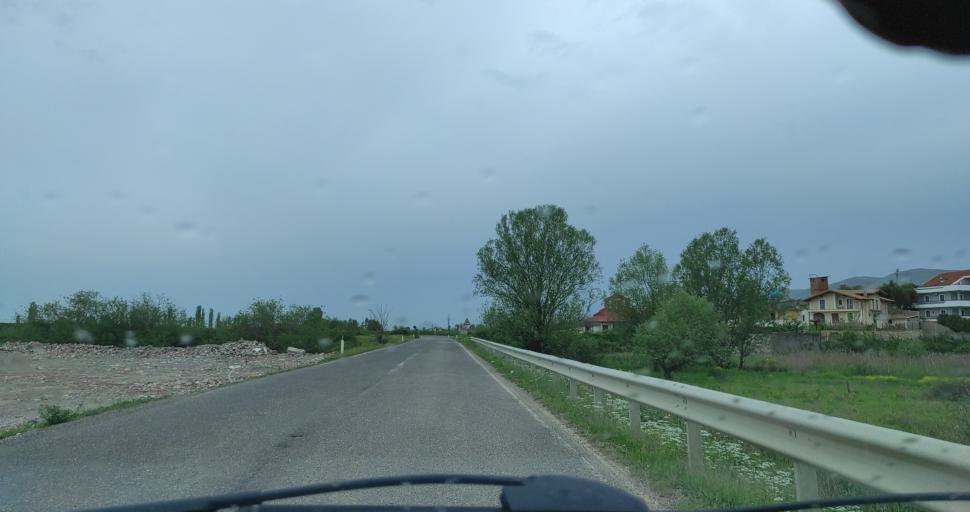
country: AL
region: Lezhe
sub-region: Rrethi i Kurbinit
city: Mamurras
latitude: 41.5934
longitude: 19.6989
